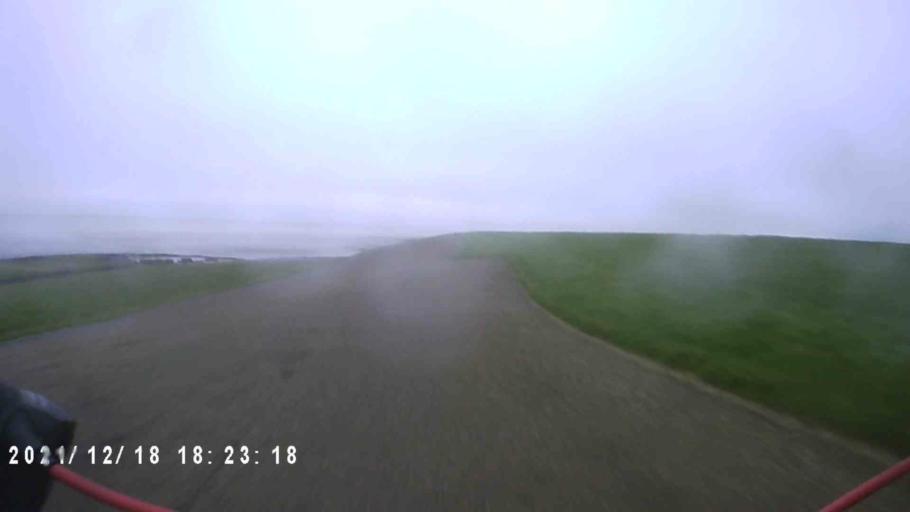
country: NL
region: Friesland
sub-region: Gemeente Dongeradeel
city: Ternaard
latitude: 53.3970
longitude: 5.9891
